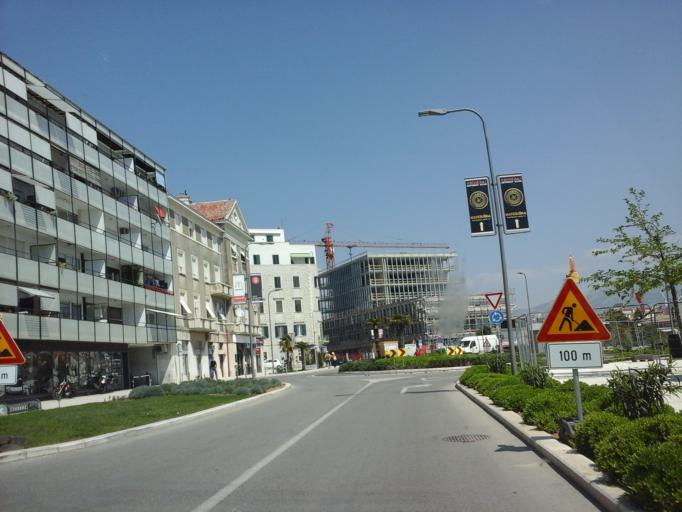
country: HR
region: Splitsko-Dalmatinska
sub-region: Grad Split
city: Split
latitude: 43.5058
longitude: 16.4316
